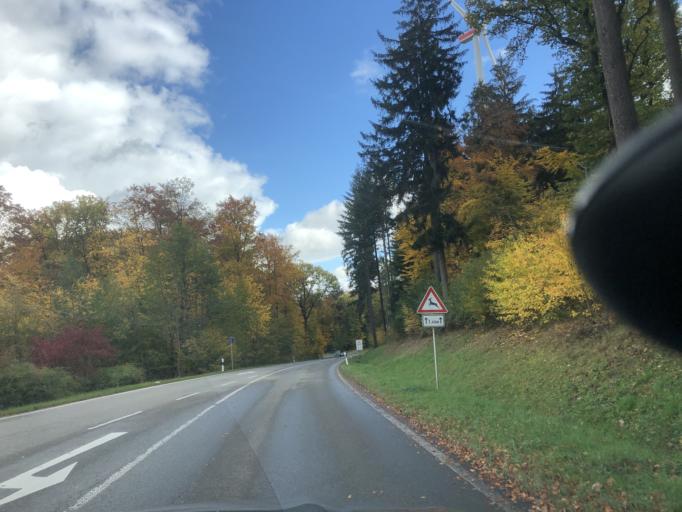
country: DE
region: Baden-Wuerttemberg
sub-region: Regierungsbezirk Stuttgart
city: Winterbach
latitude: 48.7783
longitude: 9.4623
